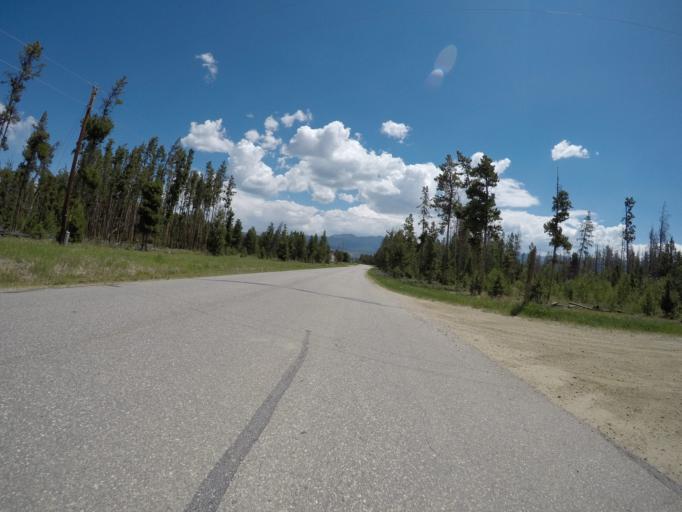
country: US
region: Colorado
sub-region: Grand County
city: Fraser
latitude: 39.9474
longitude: -105.8427
